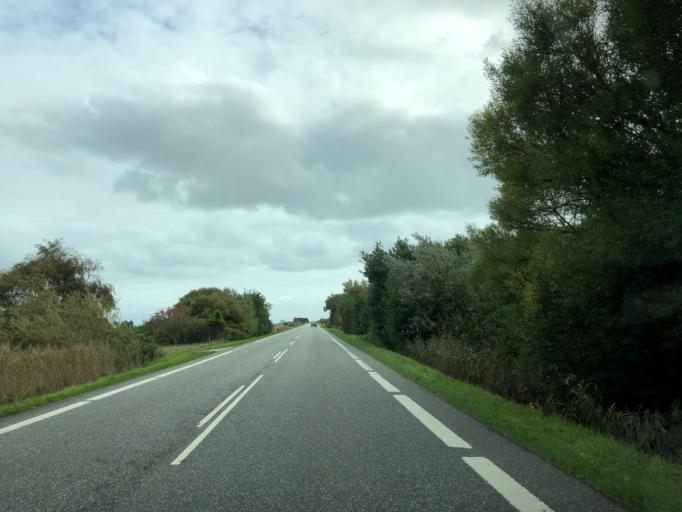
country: DK
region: North Denmark
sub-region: Thisted Kommune
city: Hurup
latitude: 56.6780
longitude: 8.3969
